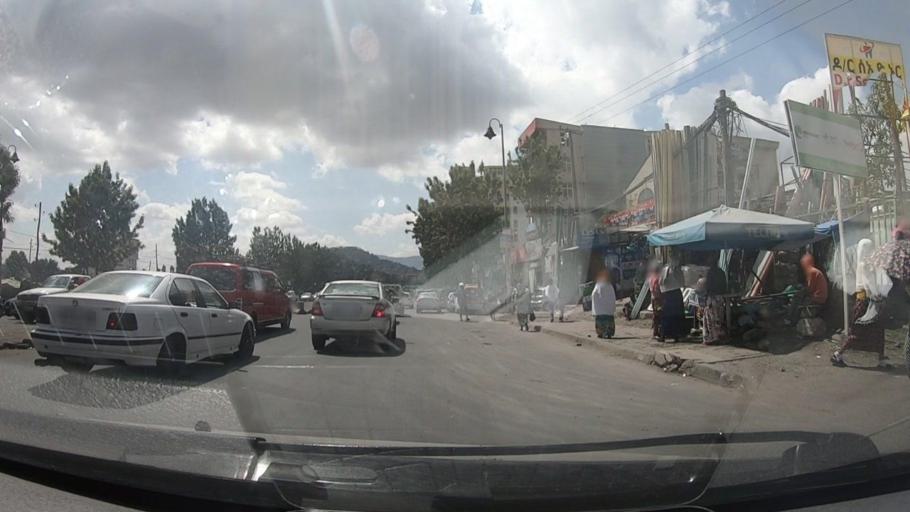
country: ET
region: Adis Abeba
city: Addis Ababa
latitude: 8.9688
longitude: 38.7216
